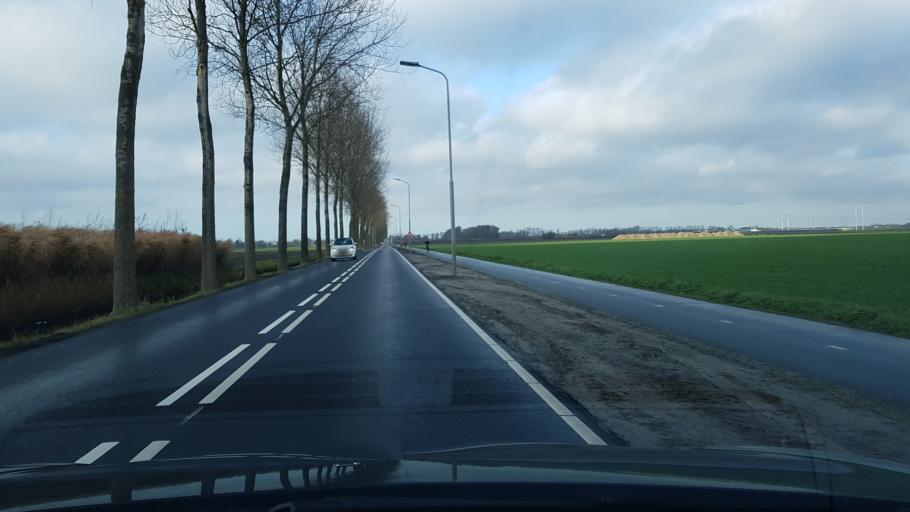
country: NL
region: South Holland
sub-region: Gemeente Lisse
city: Lisse
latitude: 52.2454
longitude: 4.6029
